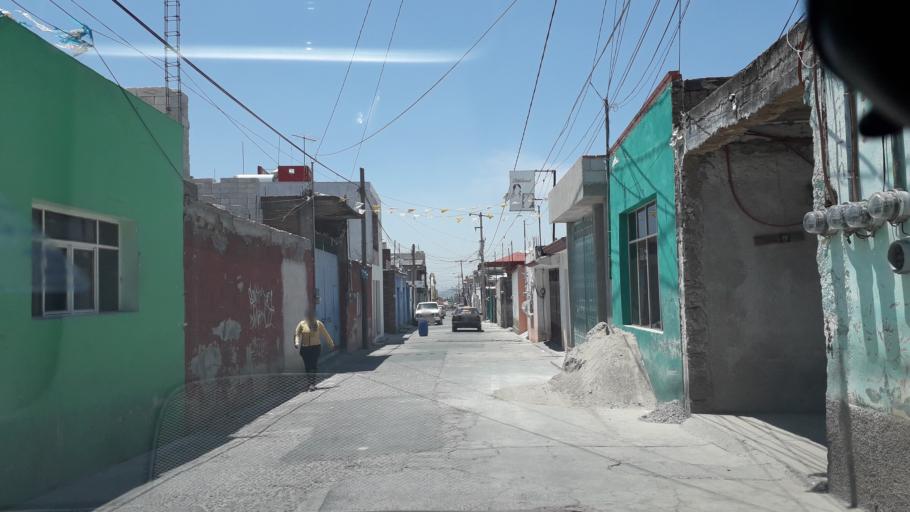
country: MX
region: Puebla
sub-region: Puebla
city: Santa Maria Xonacatepec
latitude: 19.0891
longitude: -98.1039
